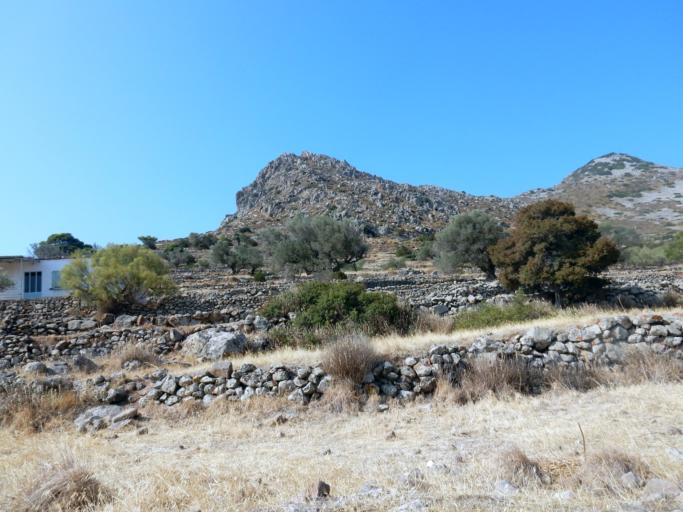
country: GR
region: Attica
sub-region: Nomos Piraios
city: Vathi
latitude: 37.7053
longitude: 23.5048
